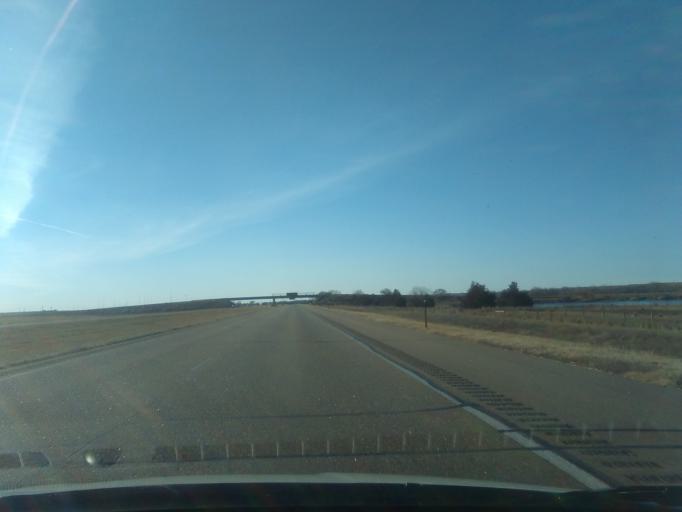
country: US
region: Colorado
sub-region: Sedgwick County
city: Julesburg
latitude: 41.0384
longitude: -102.1226
